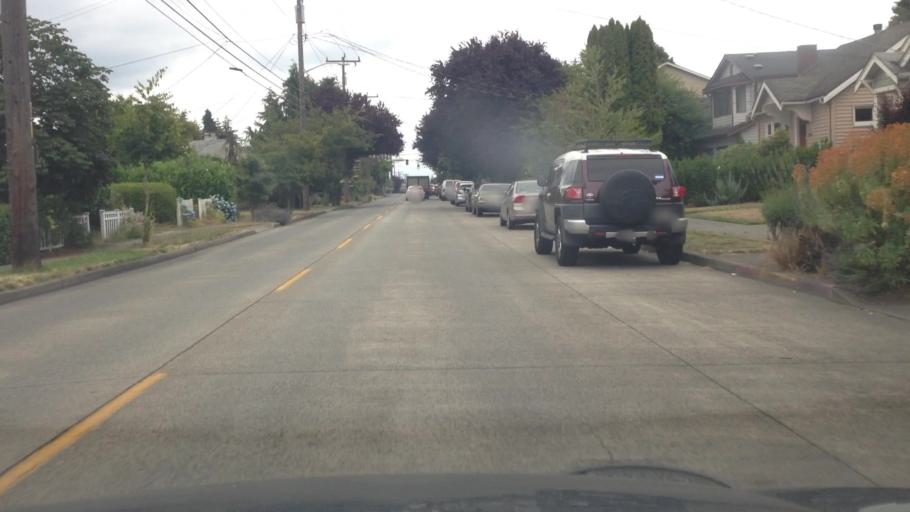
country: US
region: Washington
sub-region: King County
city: Shoreline
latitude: 47.6868
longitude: -122.3201
